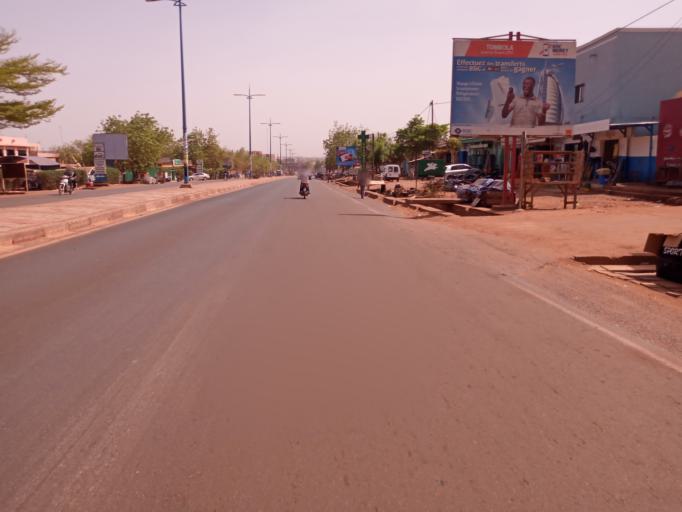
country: ML
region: Bamako
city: Bamako
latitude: 12.5863
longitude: -7.9918
